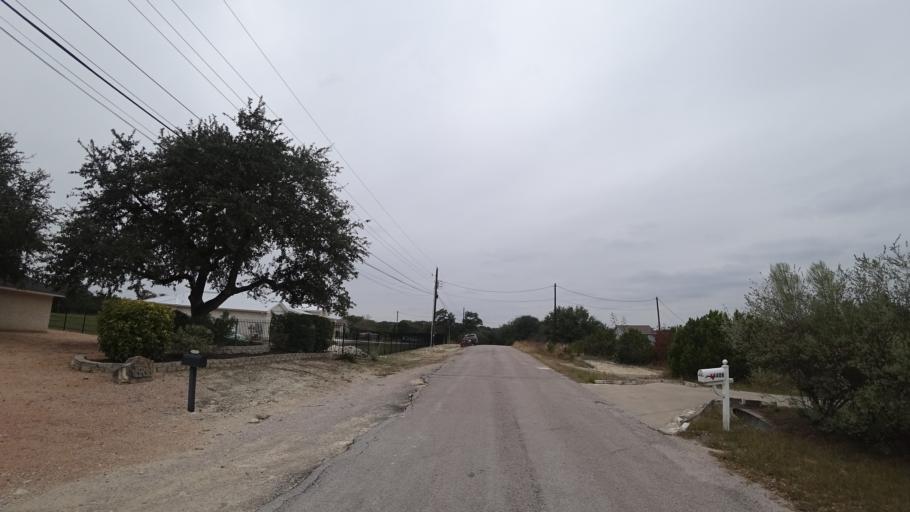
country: US
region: Texas
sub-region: Travis County
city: Lakeway
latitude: 30.3682
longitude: -97.9325
